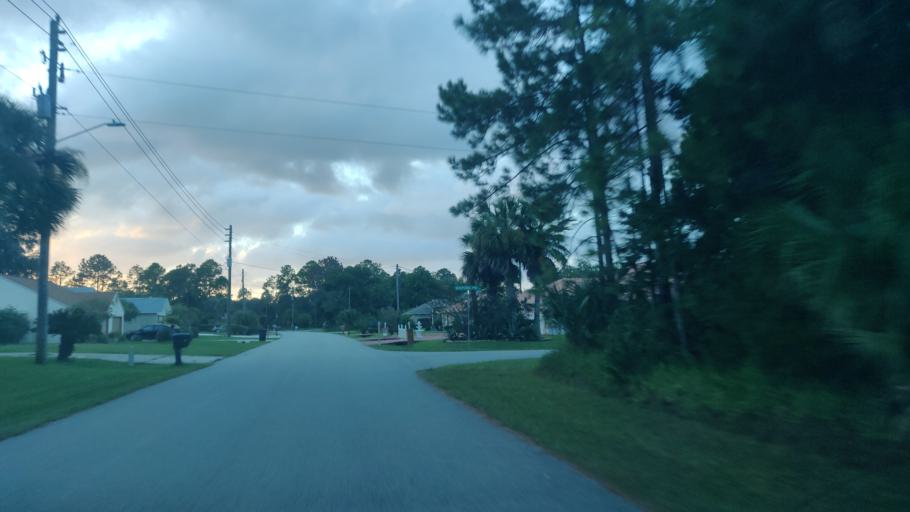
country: US
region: Florida
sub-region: Flagler County
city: Bunnell
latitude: 29.5228
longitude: -81.2320
